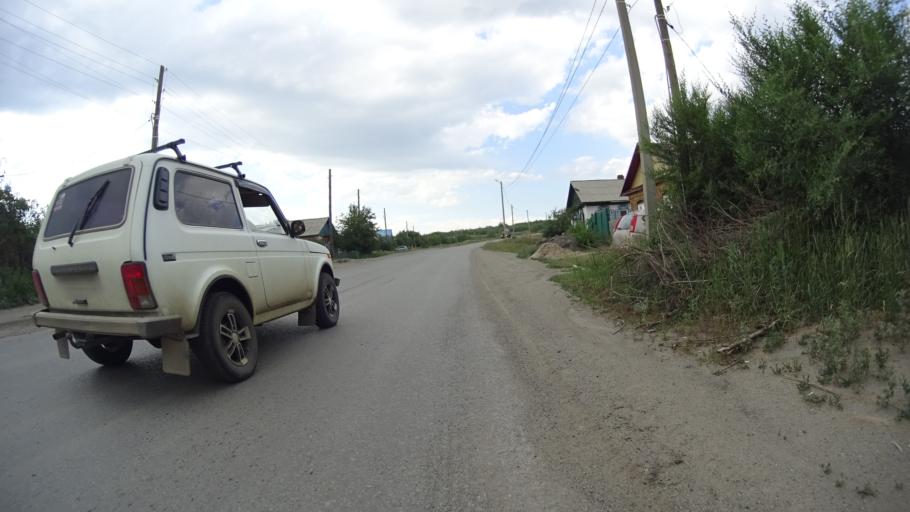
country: RU
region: Chelyabinsk
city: Troitsk
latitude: 54.0990
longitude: 61.5912
